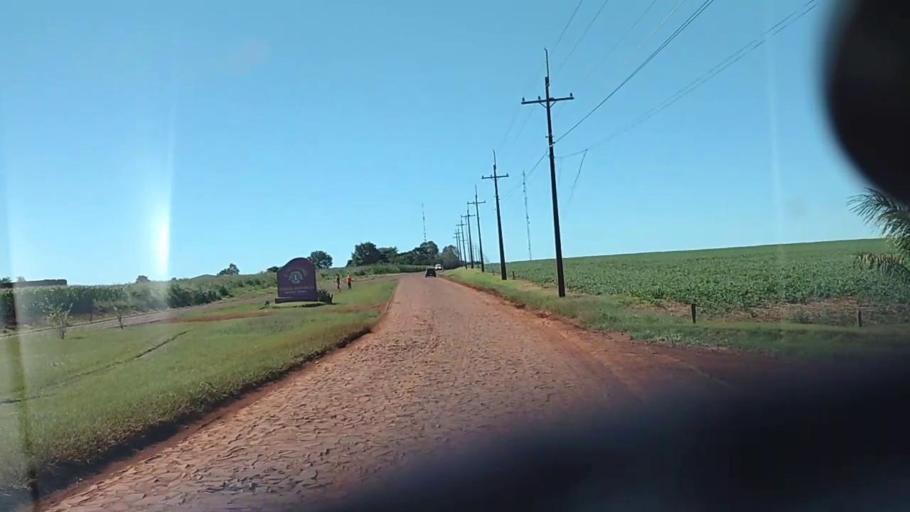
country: PY
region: Alto Parana
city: Naranjal
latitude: -25.9765
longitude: -55.1732
